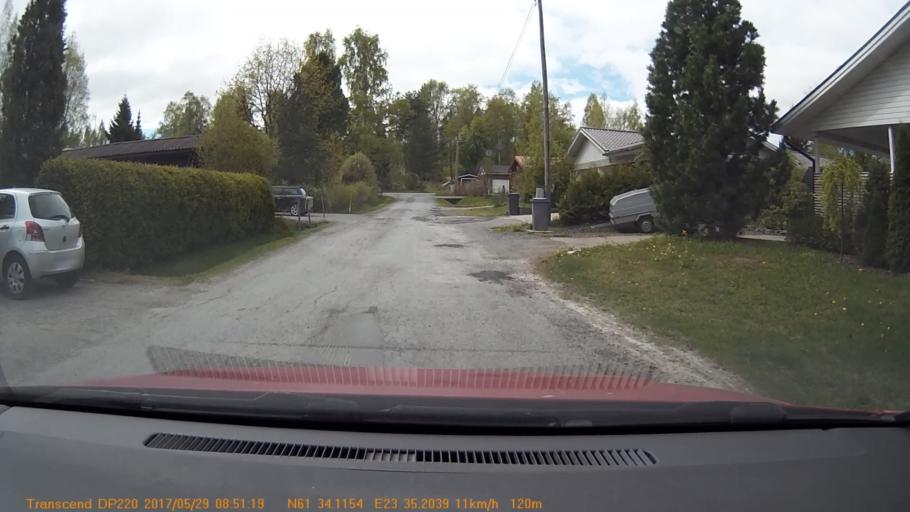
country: FI
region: Pirkanmaa
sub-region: Tampere
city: Yloejaervi
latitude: 61.5686
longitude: 23.5867
